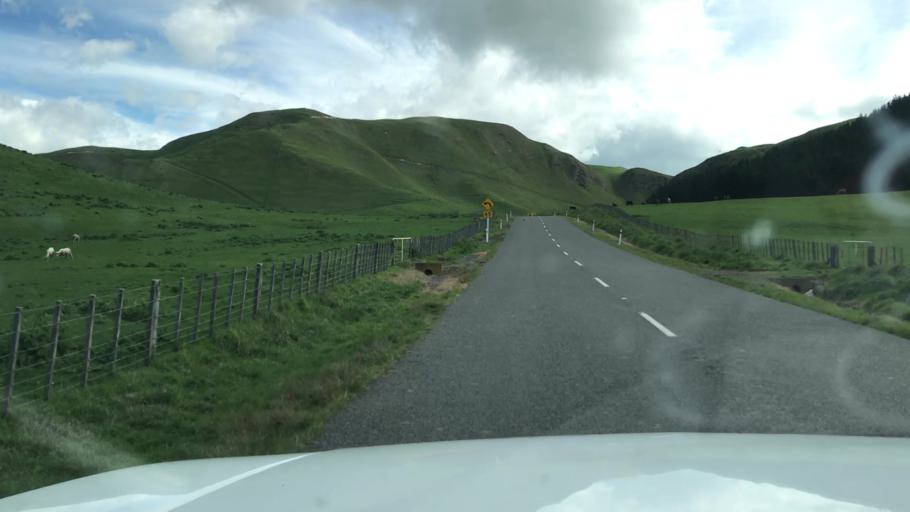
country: NZ
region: Hawke's Bay
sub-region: Hastings District
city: Hastings
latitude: -39.8215
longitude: 176.7349
